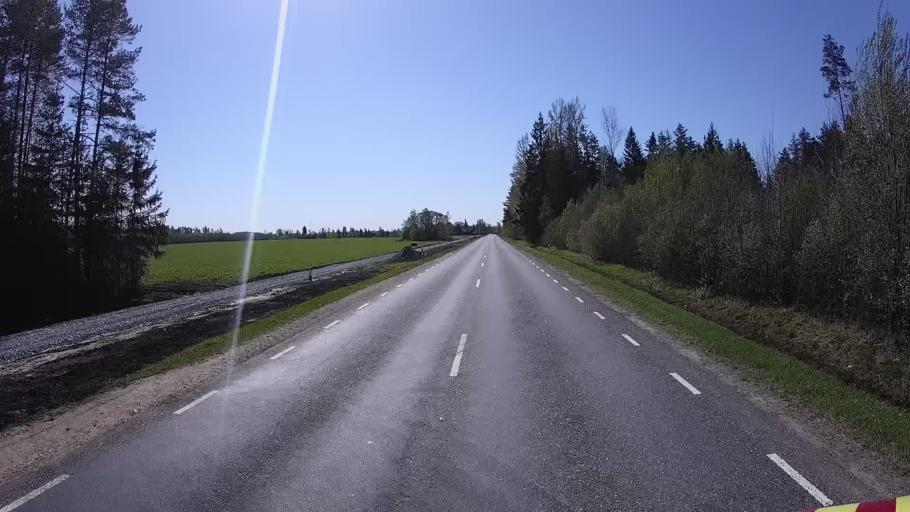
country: EE
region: Paernumaa
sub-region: Tootsi vald
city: Tootsi
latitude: 58.4956
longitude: 24.8046
